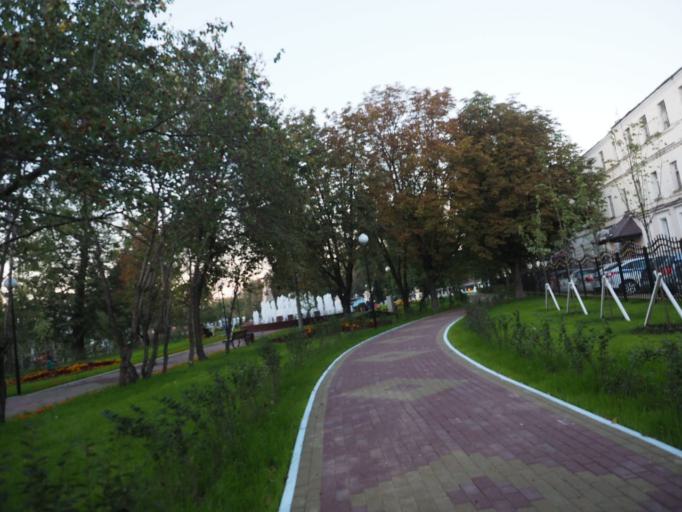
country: RU
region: Moscow
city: Lefortovo
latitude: 55.7605
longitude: 37.6865
